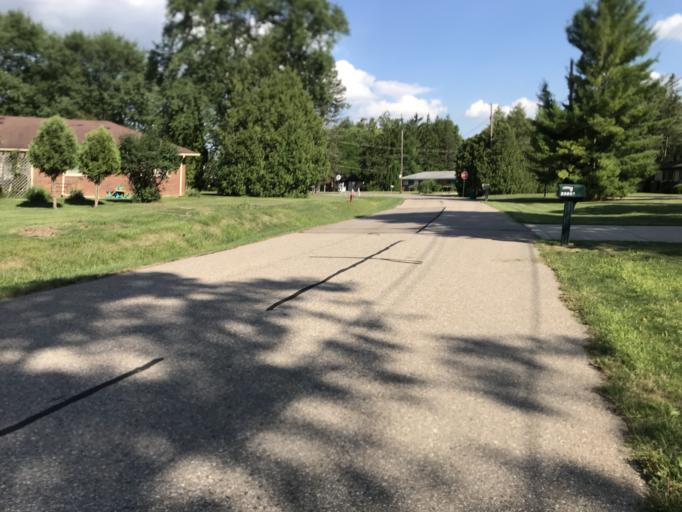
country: US
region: Michigan
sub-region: Oakland County
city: Farmington
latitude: 42.4664
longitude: -83.3255
